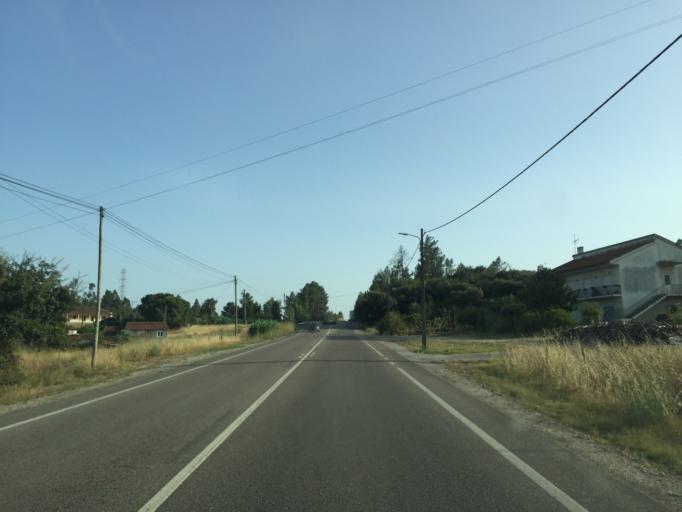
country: PT
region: Santarem
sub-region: Chamusca
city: Vila Nova da Barquinha
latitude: 39.5236
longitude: -8.4095
